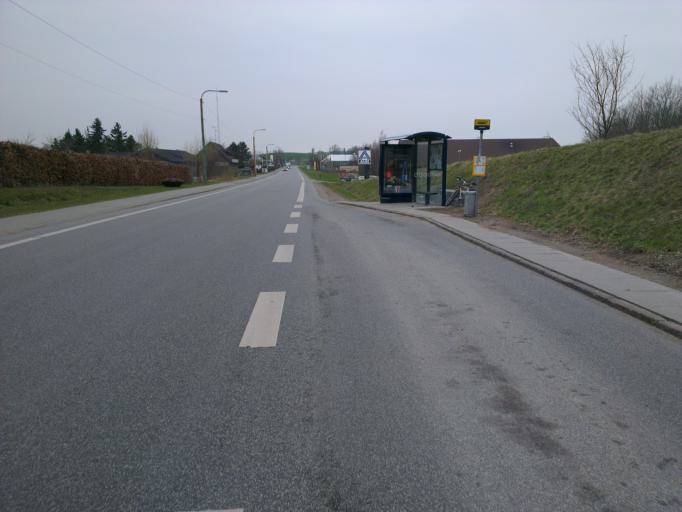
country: DK
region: Capital Region
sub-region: Frederikssund Kommune
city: Skibby
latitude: 55.7568
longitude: 11.9583
